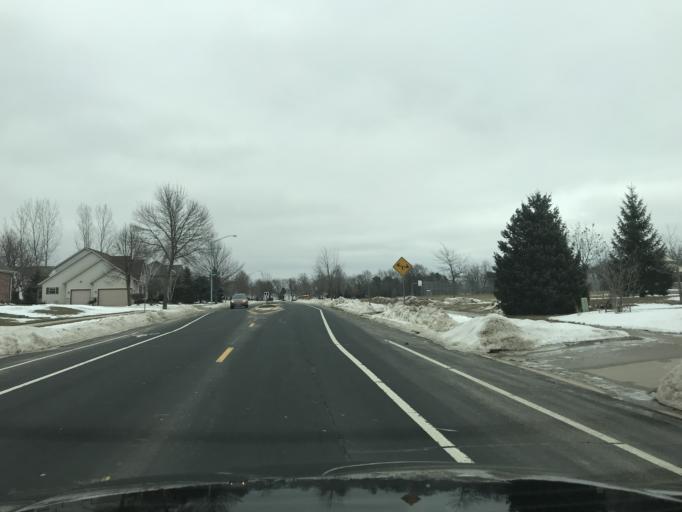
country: US
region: Wisconsin
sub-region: Dane County
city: Monona
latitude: 43.0785
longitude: -89.2749
